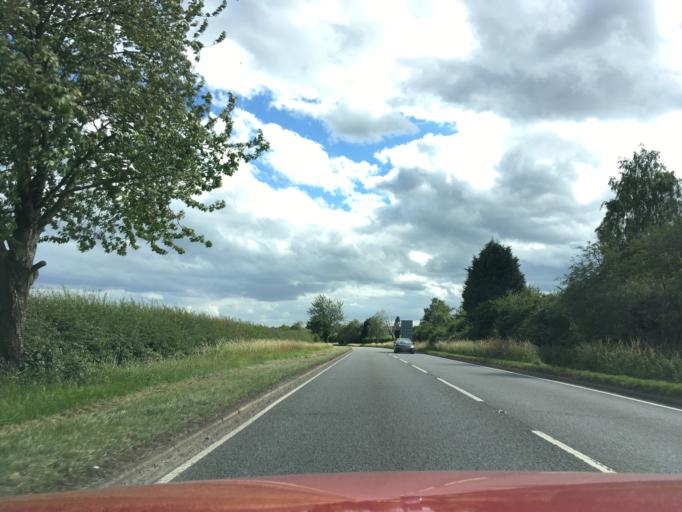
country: GB
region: England
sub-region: Warwickshire
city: Hartshill
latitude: 52.5700
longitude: -1.4815
